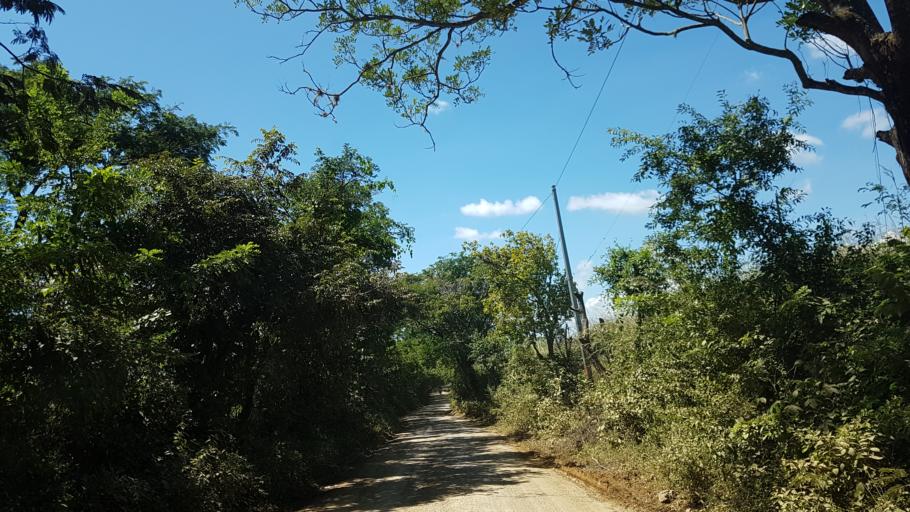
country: HN
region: El Paraiso
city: Santa Cruz
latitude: 13.7348
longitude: -86.6752
